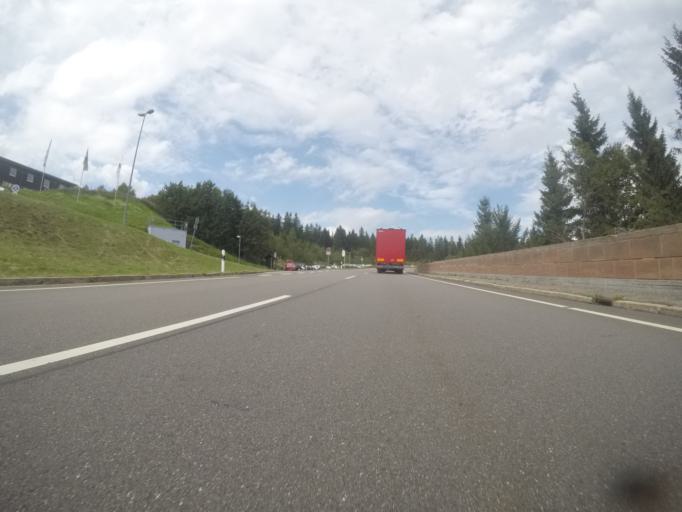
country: DE
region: Baden-Wuerttemberg
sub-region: Freiburg Region
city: Seebach
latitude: 48.5322
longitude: 8.2182
